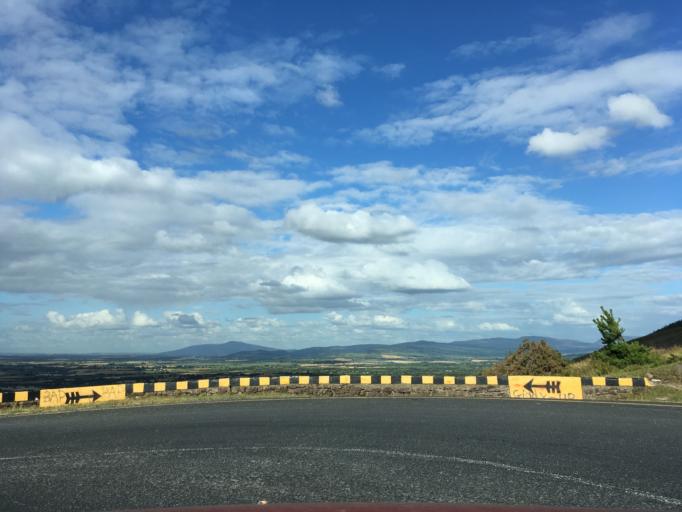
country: IE
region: Munster
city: Cahir
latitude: 52.2587
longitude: -7.9374
